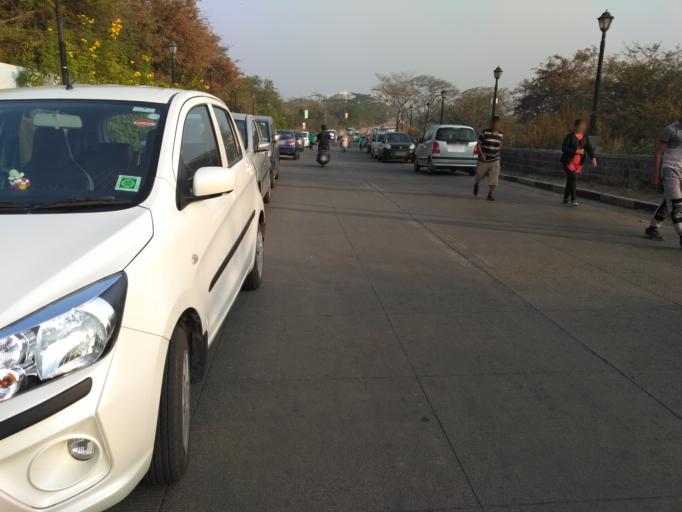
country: IN
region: Maharashtra
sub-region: Pune Division
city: Pune
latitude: 18.4770
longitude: 73.8447
